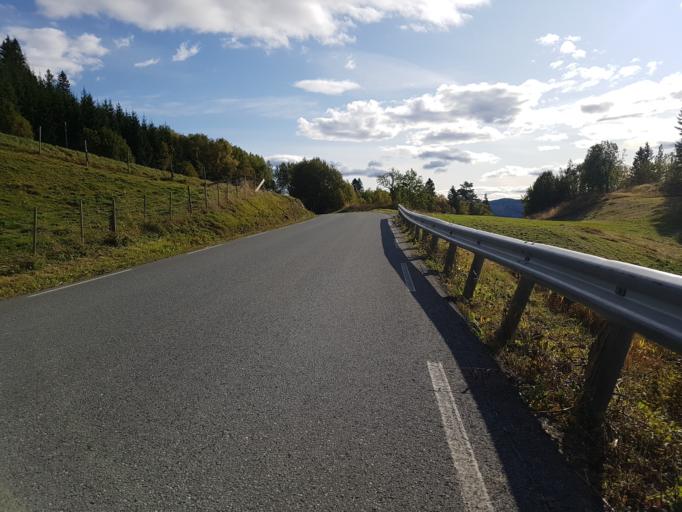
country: NO
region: Sor-Trondelag
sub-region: Malvik
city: Malvik
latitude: 63.3851
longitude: 10.5856
